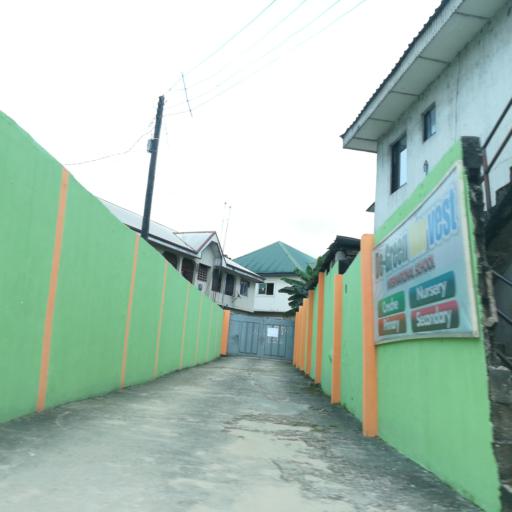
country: NG
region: Rivers
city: Port Harcourt
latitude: 4.7790
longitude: 7.0367
